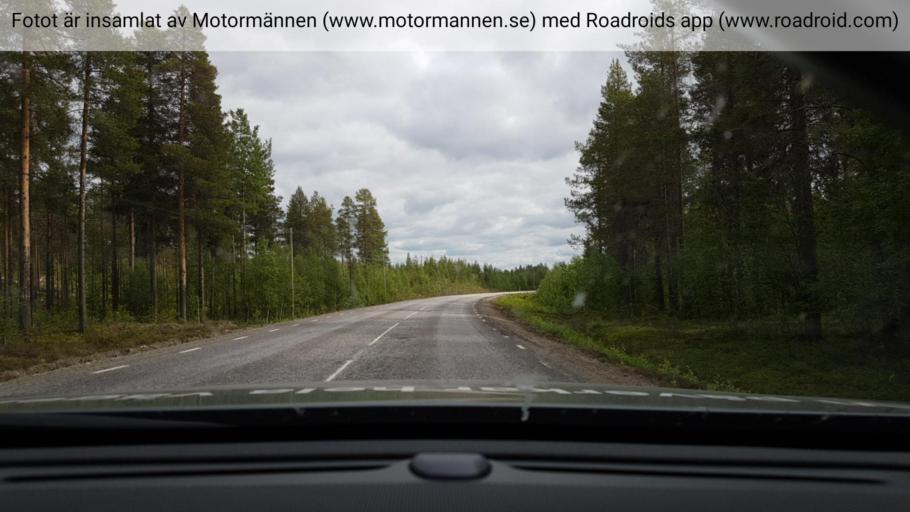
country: SE
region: Vaesterbotten
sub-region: Sorsele Kommun
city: Sorsele
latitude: 65.7818
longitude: 17.0064
